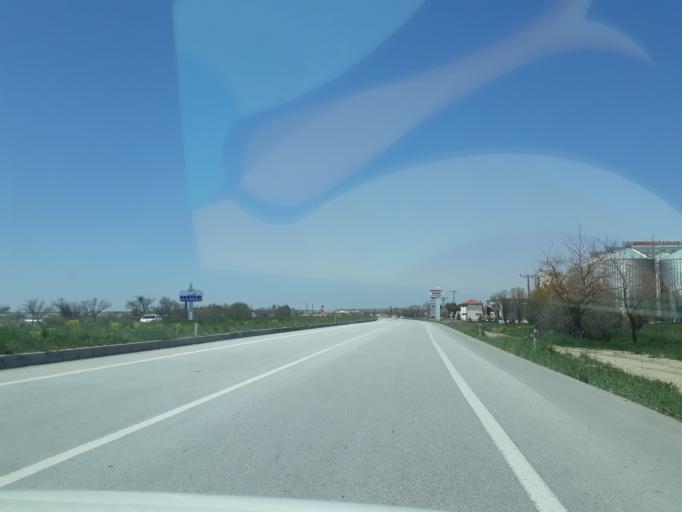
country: TR
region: Konya
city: Karapinar
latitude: 37.7156
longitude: 33.5043
